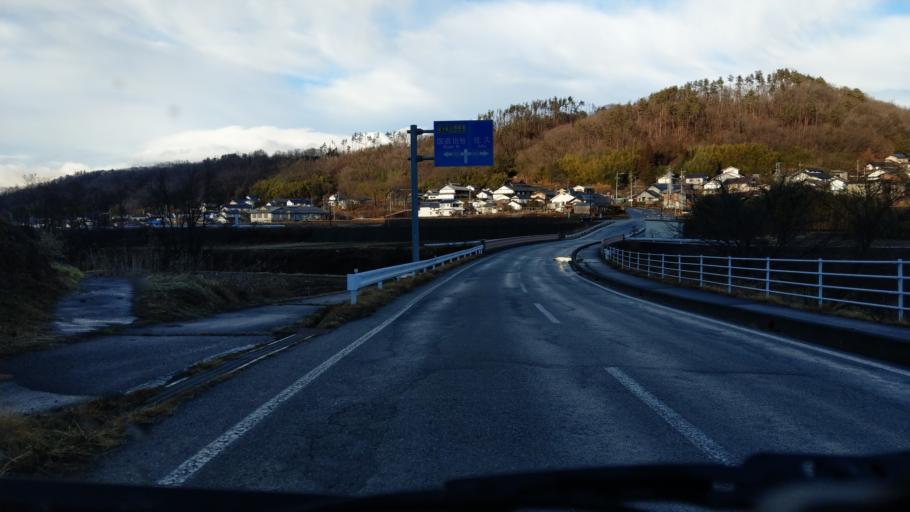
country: JP
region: Nagano
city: Kamimaruko
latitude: 36.2975
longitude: 138.3469
